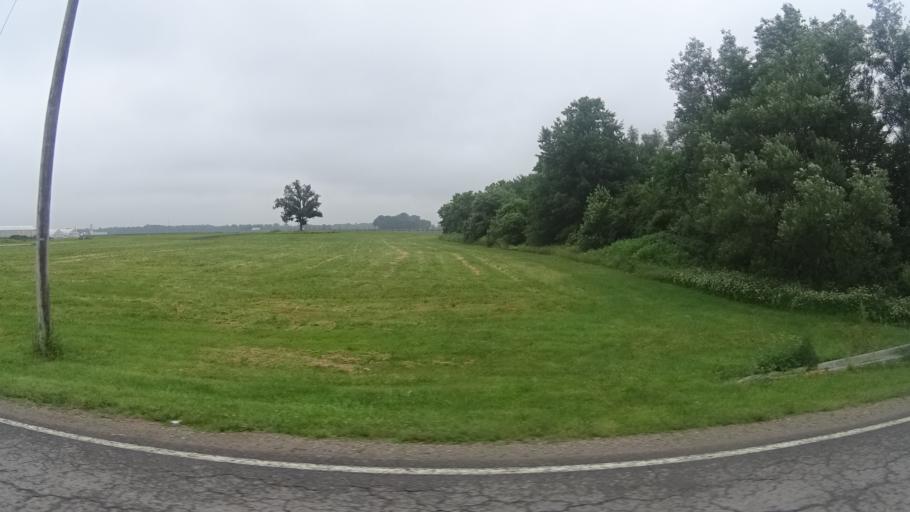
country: US
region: Ohio
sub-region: Erie County
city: Milan
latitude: 41.3587
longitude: -82.6202
